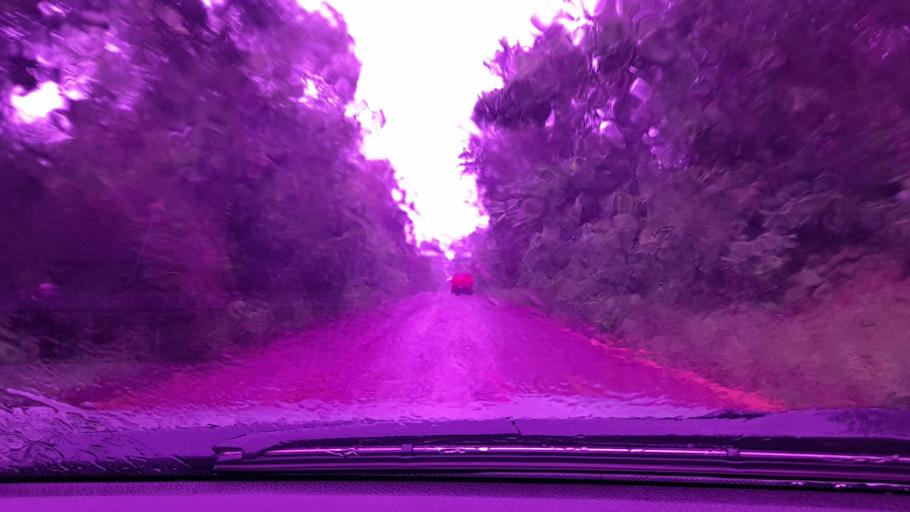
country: ET
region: Oromiya
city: Metu
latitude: 8.3452
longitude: 35.5999
